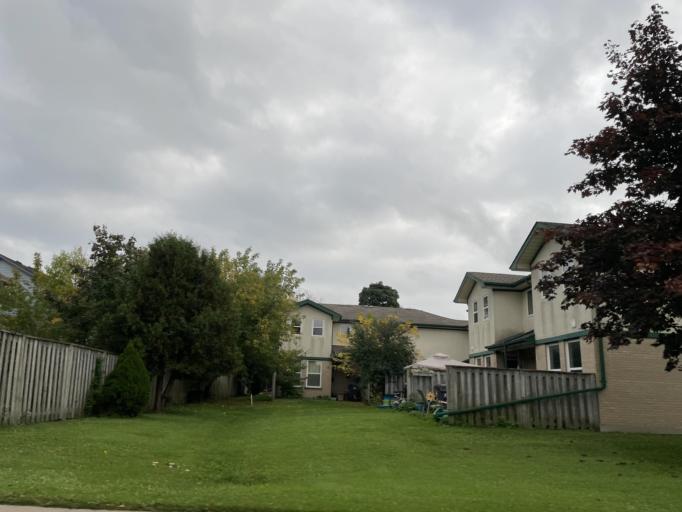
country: CA
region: Ontario
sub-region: Wellington County
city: Guelph
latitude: 43.5700
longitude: -80.2349
